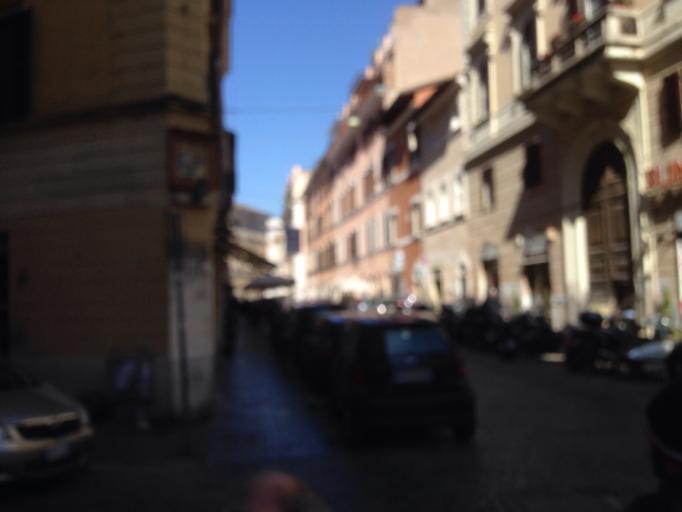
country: VA
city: Vatican City
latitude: 41.8880
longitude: 12.4713
